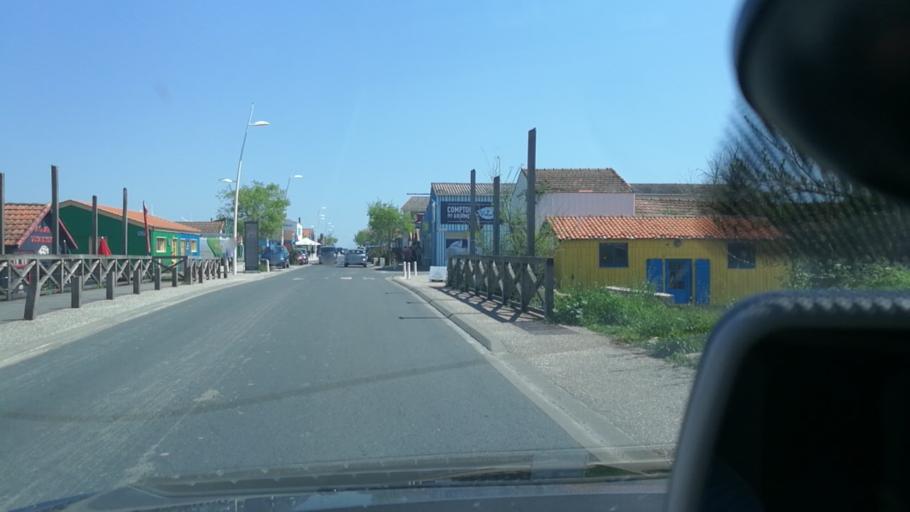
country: FR
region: Poitou-Charentes
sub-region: Departement de la Charente-Maritime
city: Saint-Trojan-les-Bains
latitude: 45.8839
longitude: -1.1940
